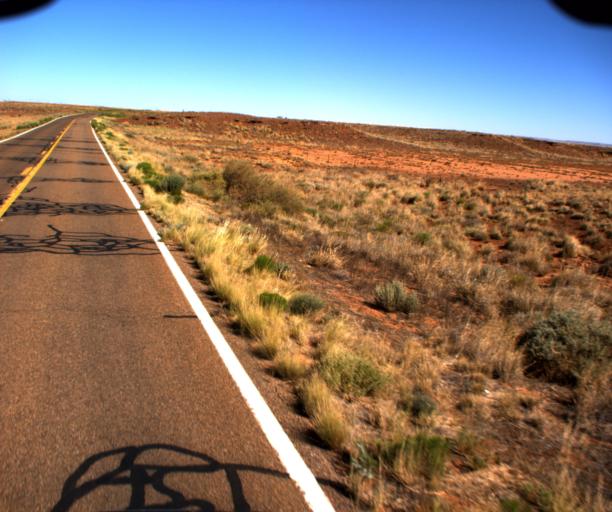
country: US
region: Arizona
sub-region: Coconino County
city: LeChee
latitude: 35.2607
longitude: -110.9676
